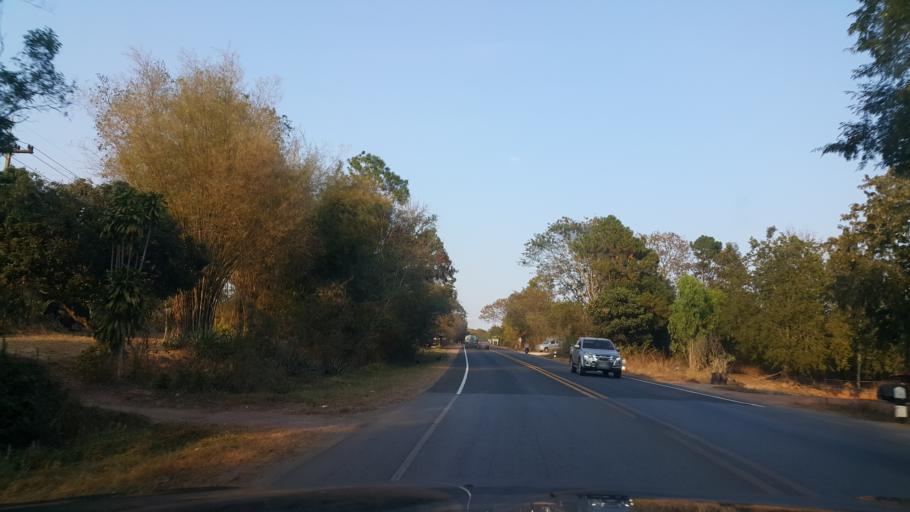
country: TH
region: Loei
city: Phu Ruea
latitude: 17.4641
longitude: 101.5113
